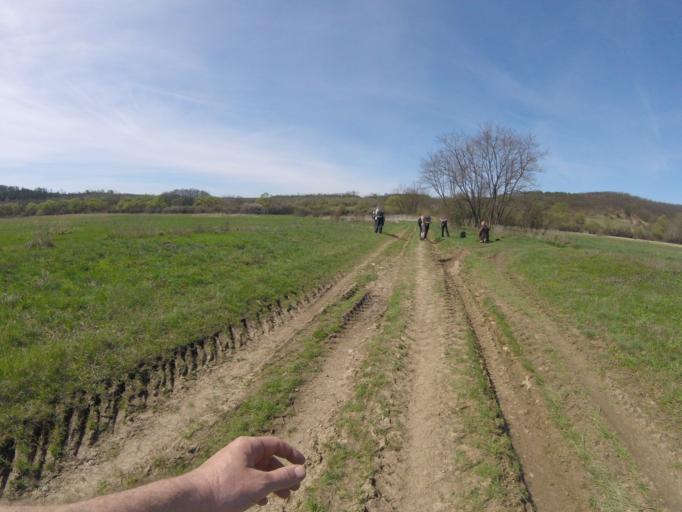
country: HU
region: Borsod-Abauj-Zemplen
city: Szendro
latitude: 48.4193
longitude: 20.7594
